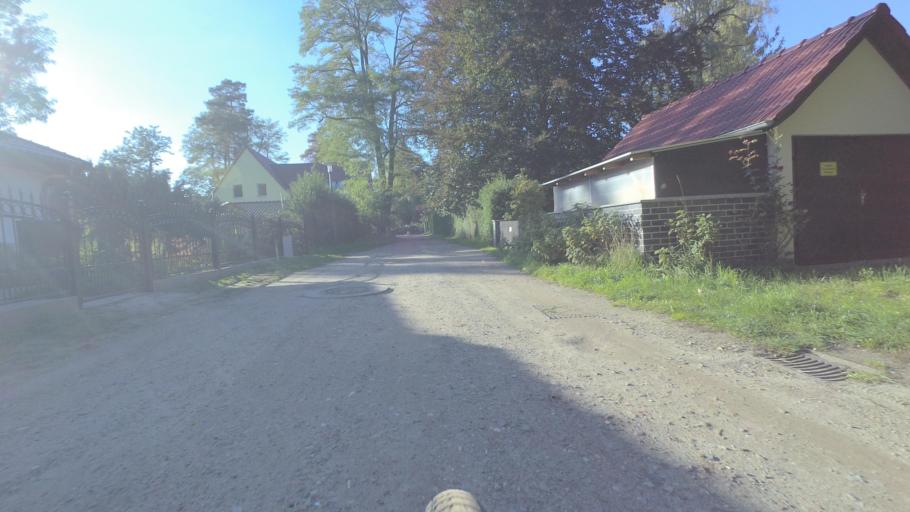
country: DE
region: Brandenburg
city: Rangsdorf
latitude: 52.3323
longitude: 13.4113
